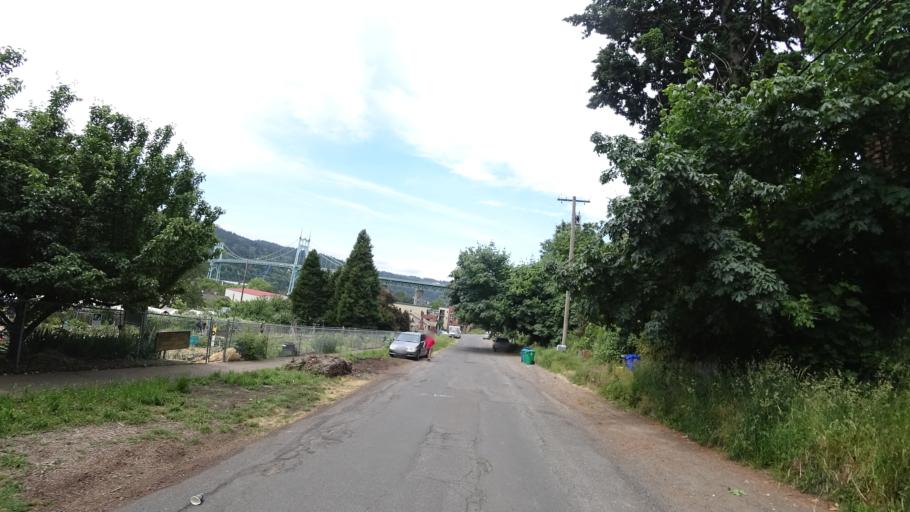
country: US
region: Oregon
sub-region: Washington County
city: West Haven
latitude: 45.5864
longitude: -122.7552
